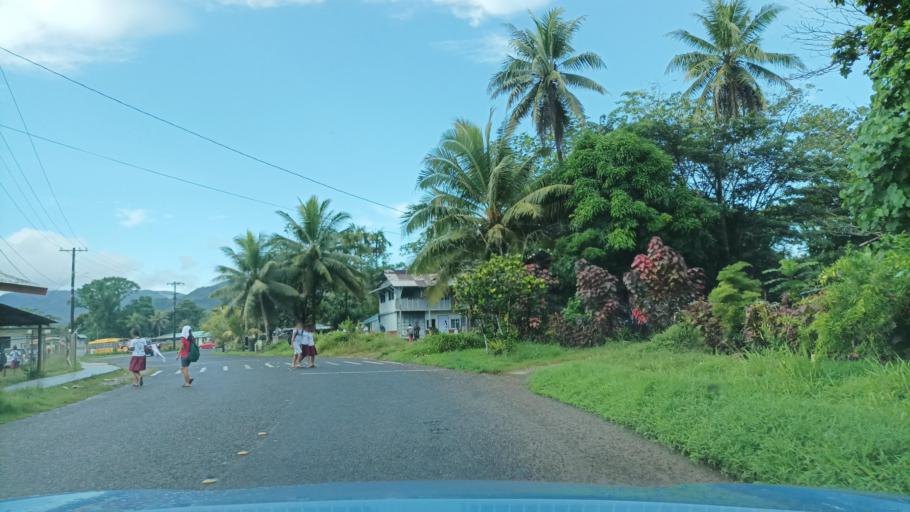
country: FM
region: Pohnpei
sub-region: Kolonia Municipality
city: Kolonia
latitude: 6.9528
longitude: 158.2069
